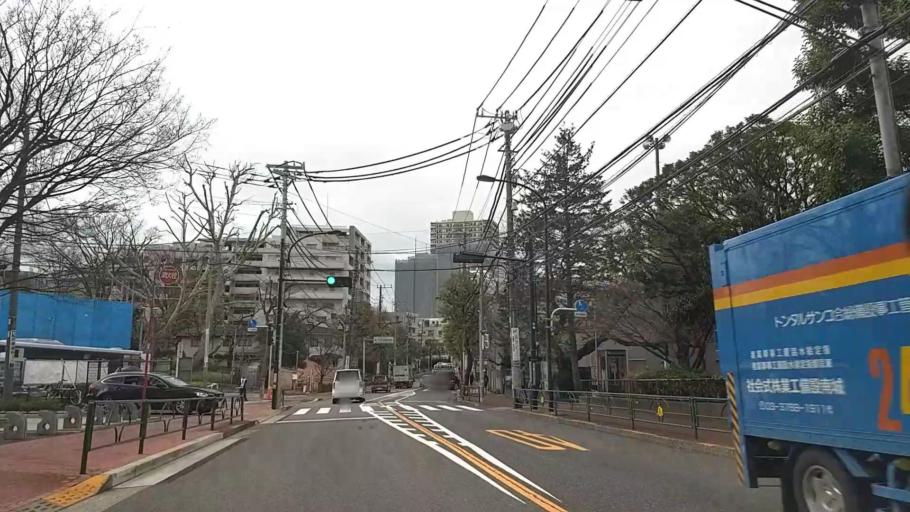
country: JP
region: Kanagawa
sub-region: Kawasaki-shi
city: Kawasaki
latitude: 35.5940
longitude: 139.7296
